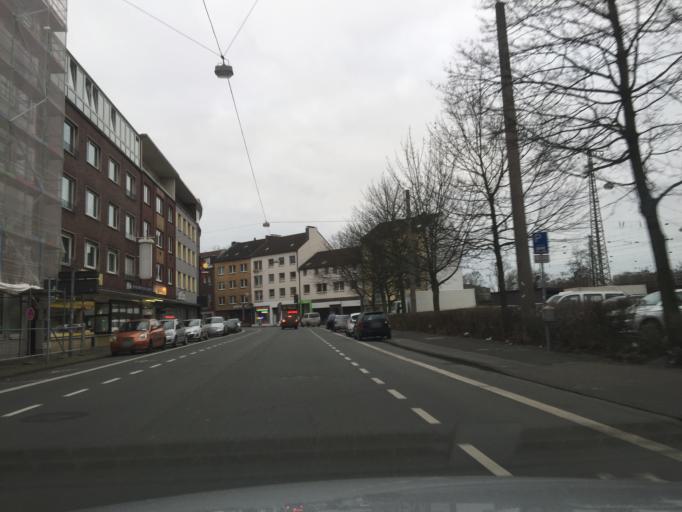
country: DE
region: North Rhine-Westphalia
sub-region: Regierungsbezirk Dusseldorf
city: Oberhausen
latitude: 51.4721
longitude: 6.8504
